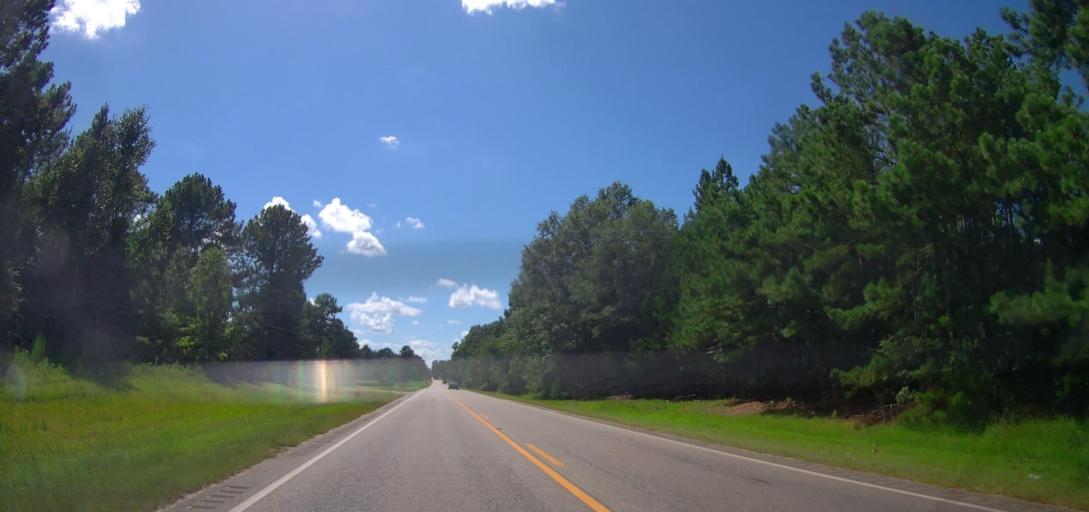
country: US
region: Alabama
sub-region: Elmore County
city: Tallassee
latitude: 32.3764
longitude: -85.8516
